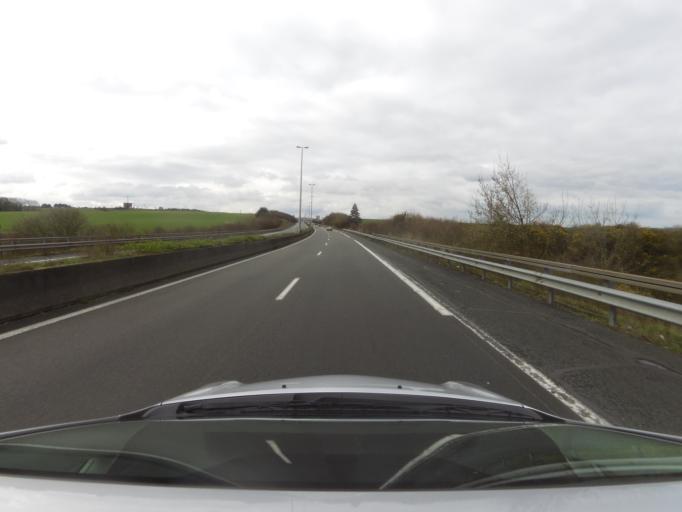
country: FR
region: Nord-Pas-de-Calais
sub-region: Departement du Pas-de-Calais
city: Marquise
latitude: 50.8330
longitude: 1.7034
